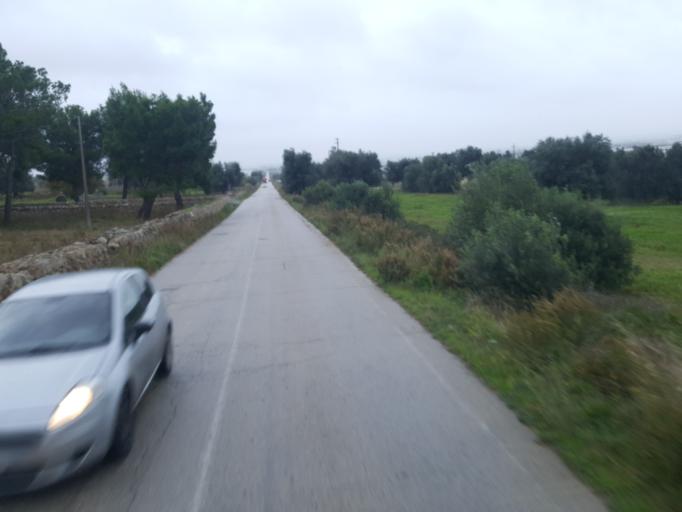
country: IT
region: Apulia
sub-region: Provincia di Taranto
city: Montemesola
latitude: 40.5492
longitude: 17.3540
